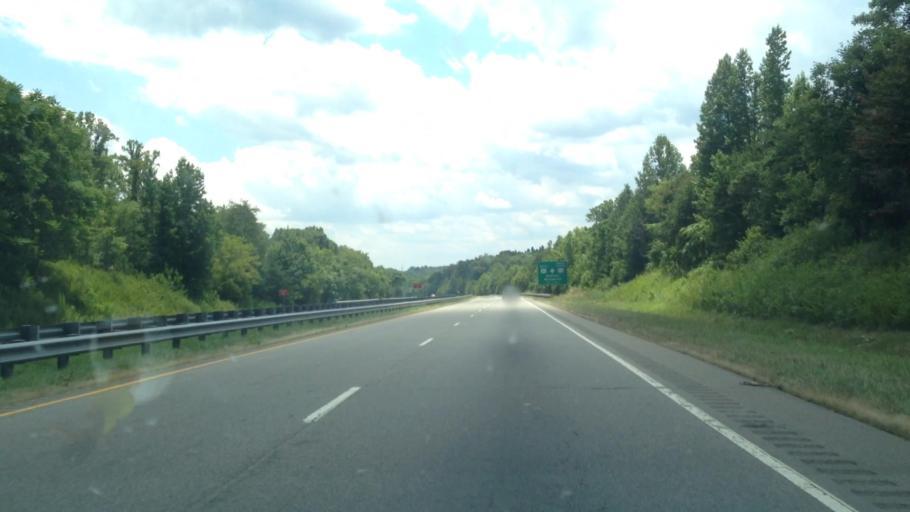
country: US
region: North Carolina
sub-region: Rockingham County
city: Madison
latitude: 36.3967
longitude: -79.9401
